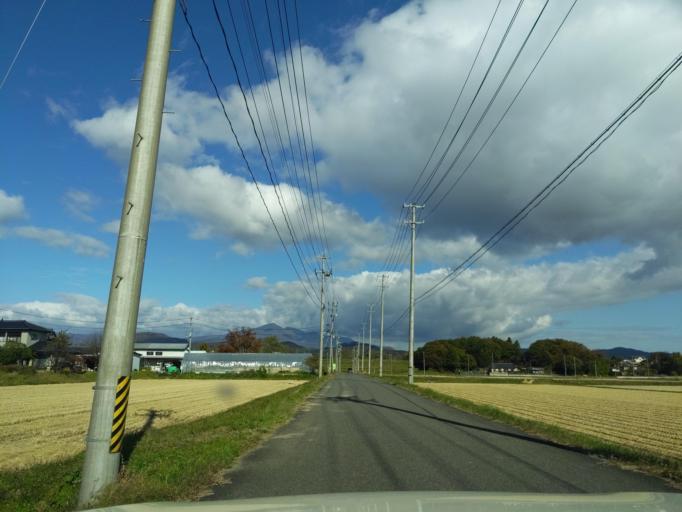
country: JP
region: Fukushima
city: Koriyama
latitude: 37.4527
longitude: 140.3206
